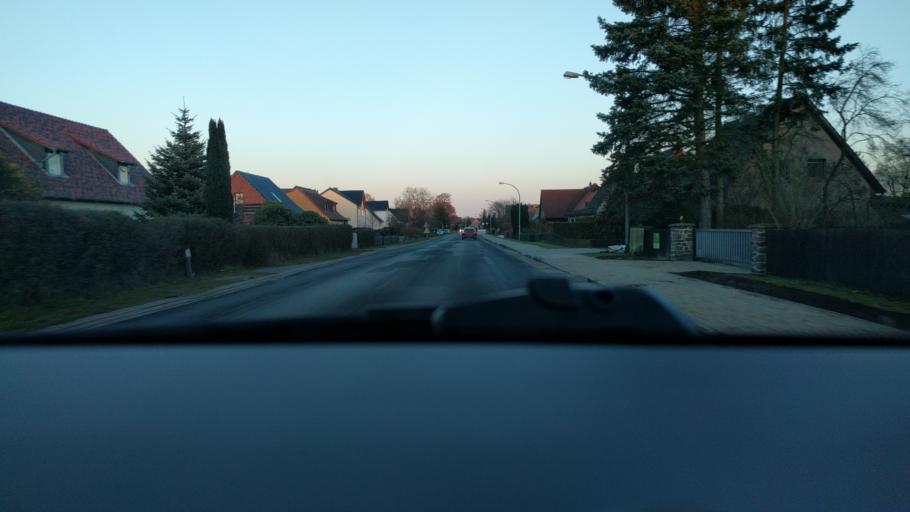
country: DE
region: Lower Saxony
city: Bokensdorf
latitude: 52.5492
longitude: 10.7058
